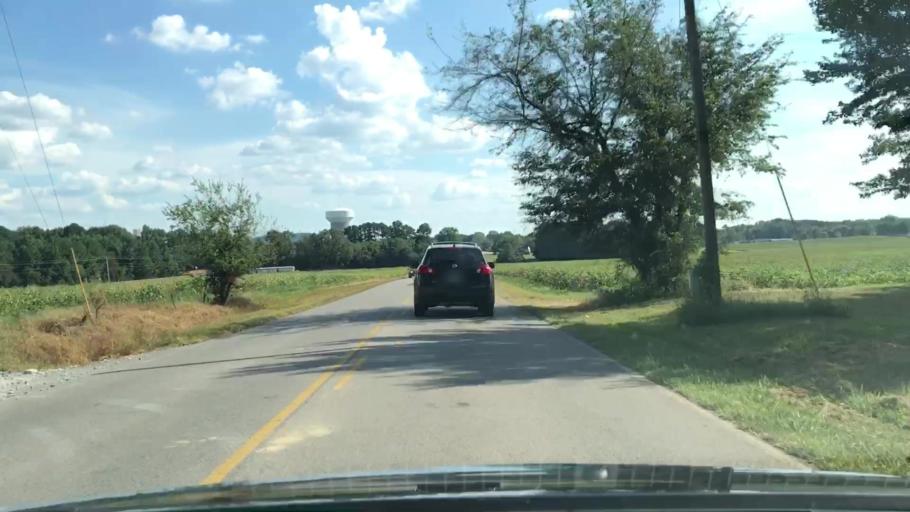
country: US
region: Alabama
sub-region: Madison County
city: Harvest
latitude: 34.8675
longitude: -86.7489
